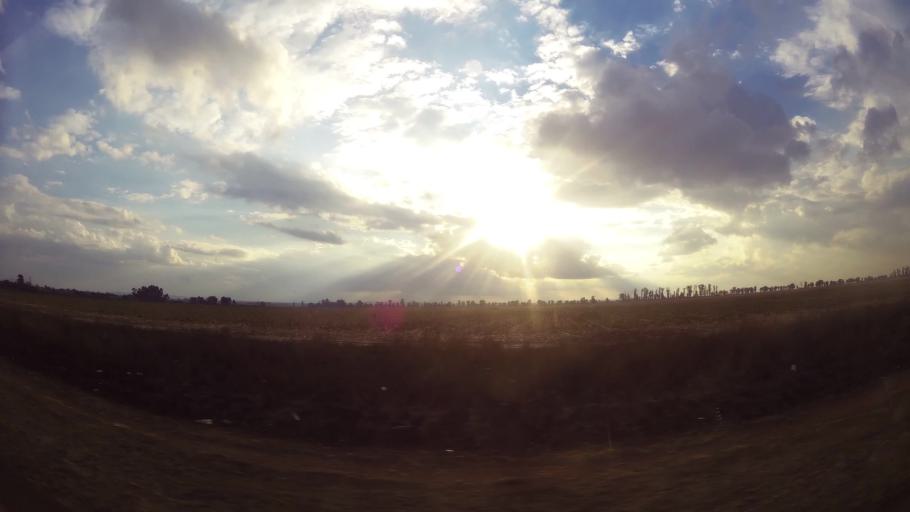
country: ZA
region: Gauteng
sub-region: Sedibeng District Municipality
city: Vanderbijlpark
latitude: -26.6583
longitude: 27.8006
